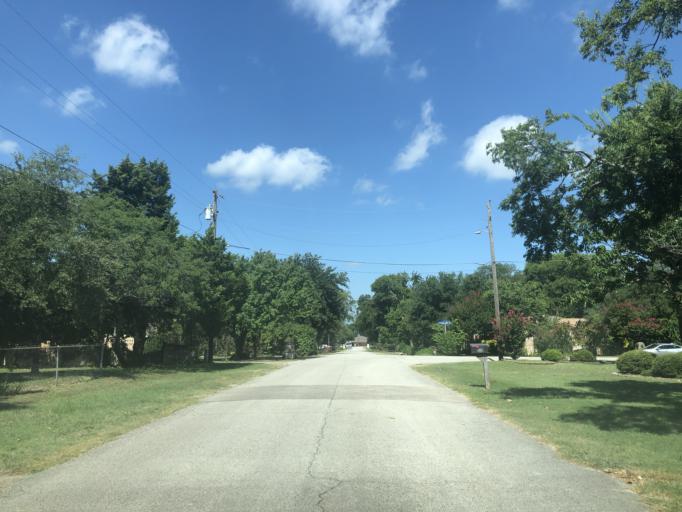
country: US
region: Texas
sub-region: Dallas County
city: Duncanville
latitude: 32.6482
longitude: -96.9350
